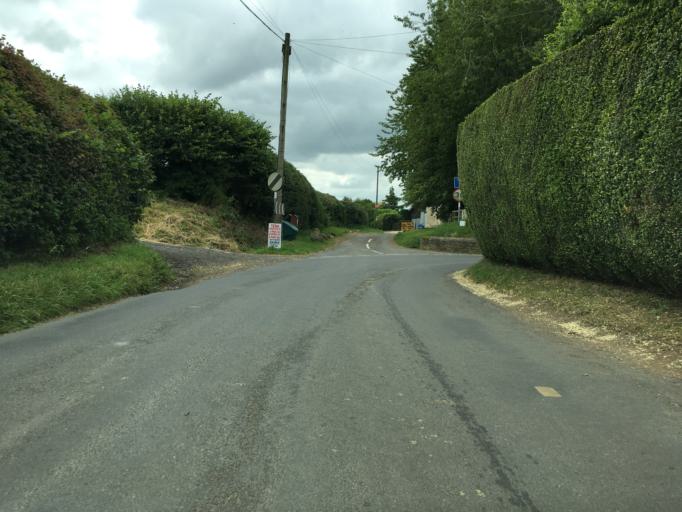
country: GB
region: England
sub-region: Oxfordshire
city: Shipton under Wychwood
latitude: 51.8947
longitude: -1.6392
